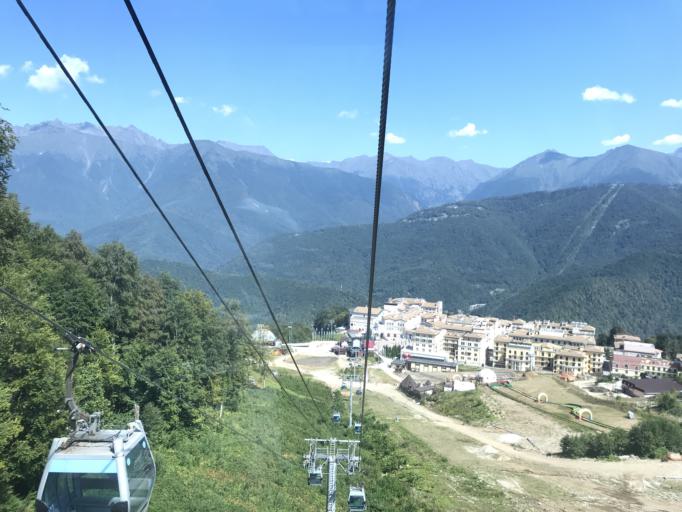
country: RU
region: Krasnodarskiy
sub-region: Sochi City
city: Krasnaya Polyana
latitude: 43.6655
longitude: 40.2563
